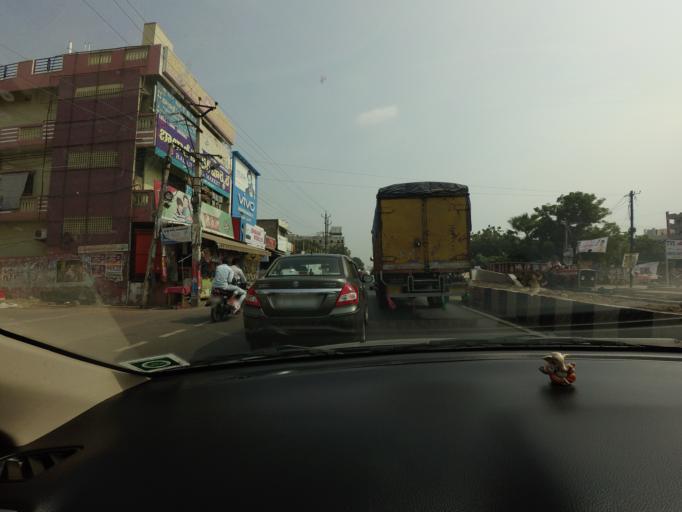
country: IN
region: Andhra Pradesh
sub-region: Krishna
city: Yanamalakuduru
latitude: 16.4863
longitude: 80.6803
